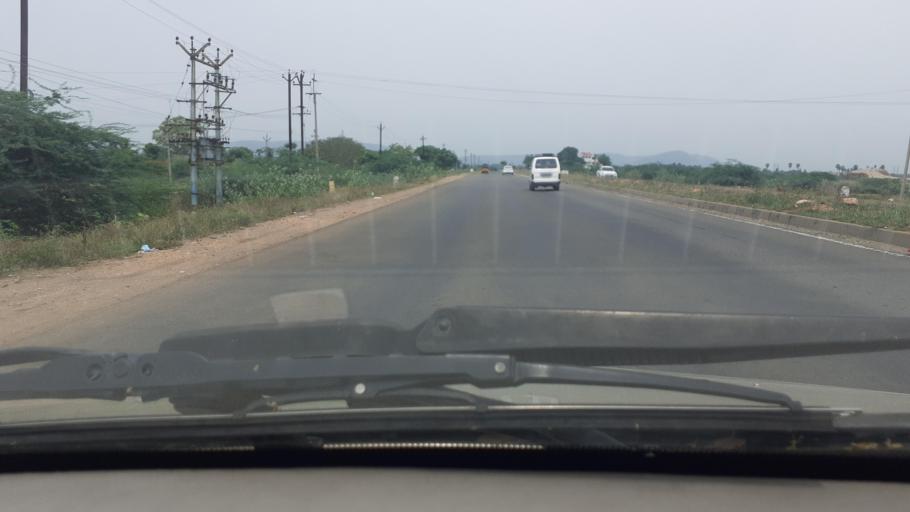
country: IN
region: Tamil Nadu
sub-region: Tirunelveli Kattabo
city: Tirunelveli
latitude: 8.7120
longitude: 77.8011
